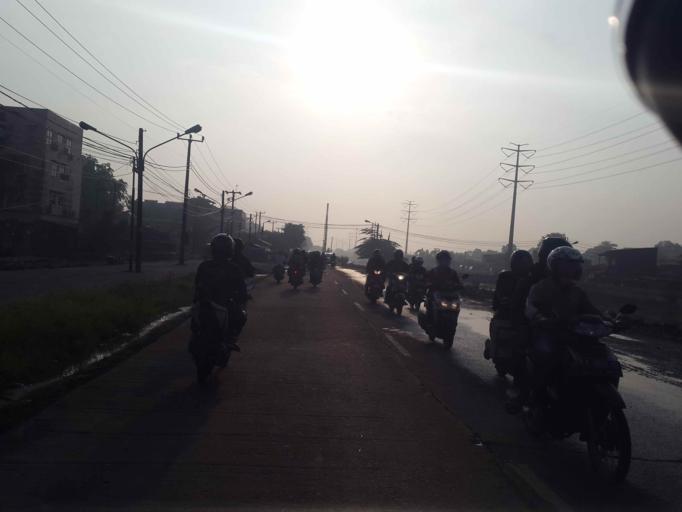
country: ID
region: West Java
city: Bekasi
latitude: -6.2623
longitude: 107.0222
